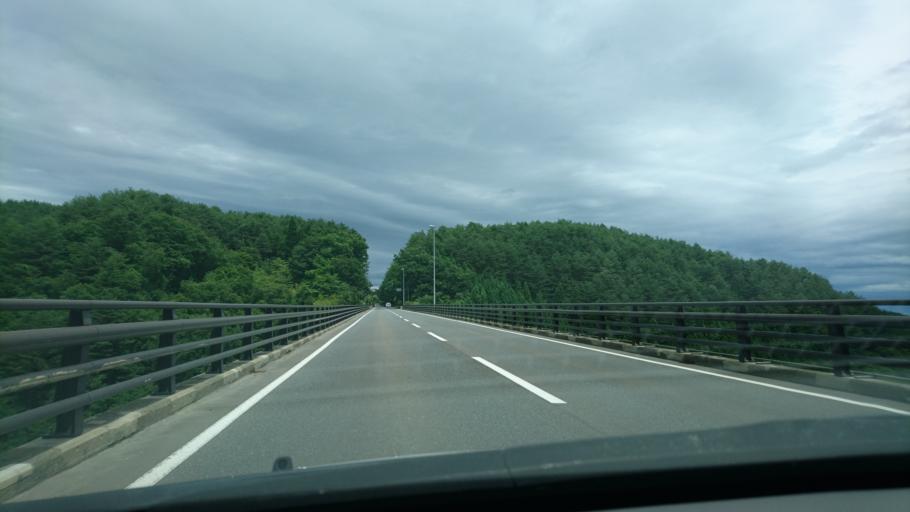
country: JP
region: Iwate
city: Miyako
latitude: 39.7083
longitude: 141.9637
